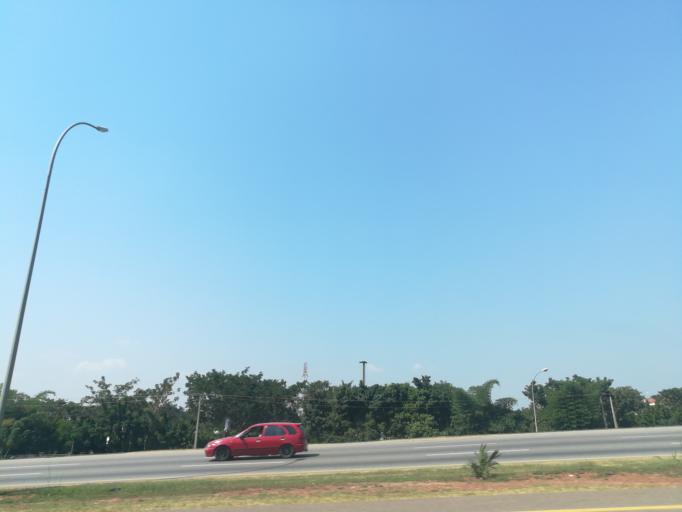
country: NG
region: Abuja Federal Capital Territory
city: Abuja
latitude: 9.0658
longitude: 7.4522
